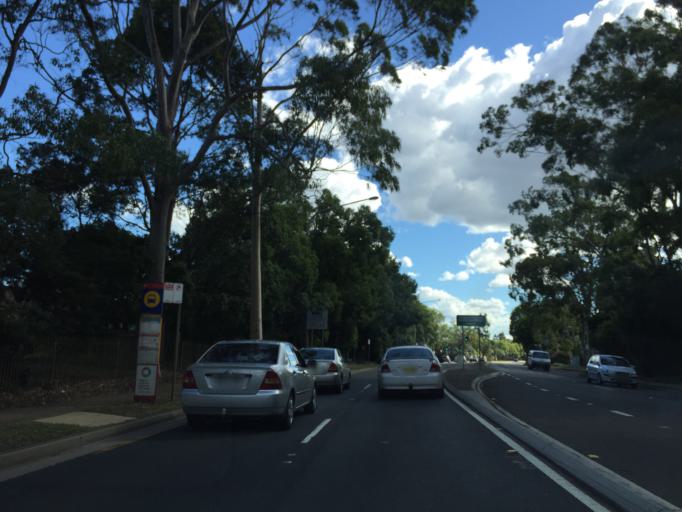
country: AU
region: New South Wales
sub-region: Parramatta
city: Telopea
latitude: -33.7929
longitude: 151.0195
